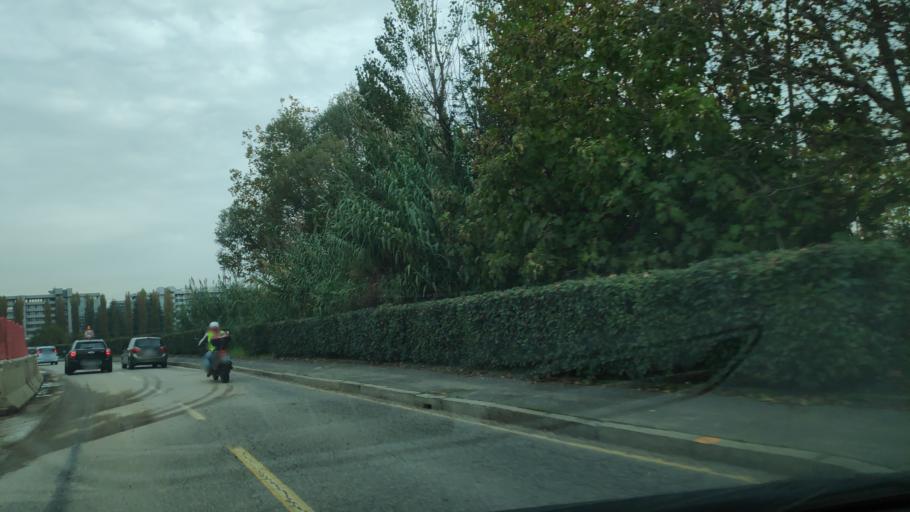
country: IT
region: Lombardy
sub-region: Citta metropolitana di Milano
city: Rozzano
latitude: 45.4046
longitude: 9.1753
